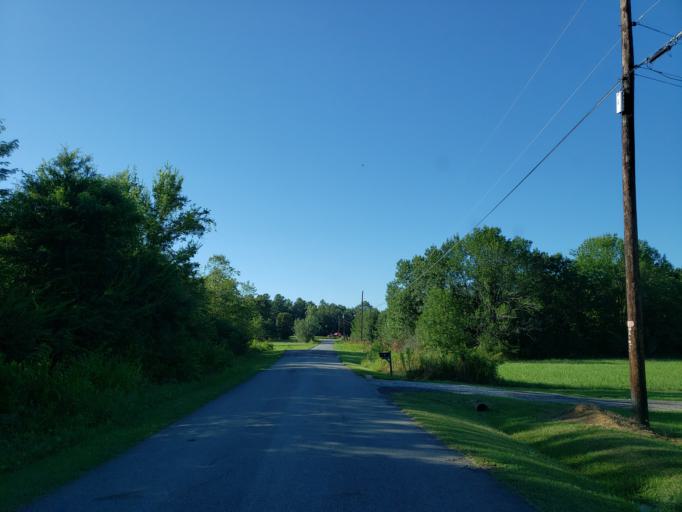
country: US
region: Georgia
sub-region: Bartow County
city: Euharlee
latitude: 34.1233
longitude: -85.0013
